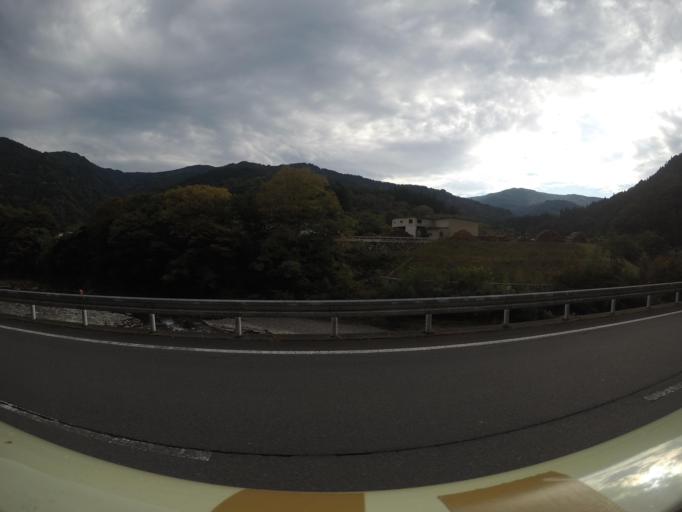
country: JP
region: Gunma
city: Yoshii
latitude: 36.1217
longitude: 138.9345
